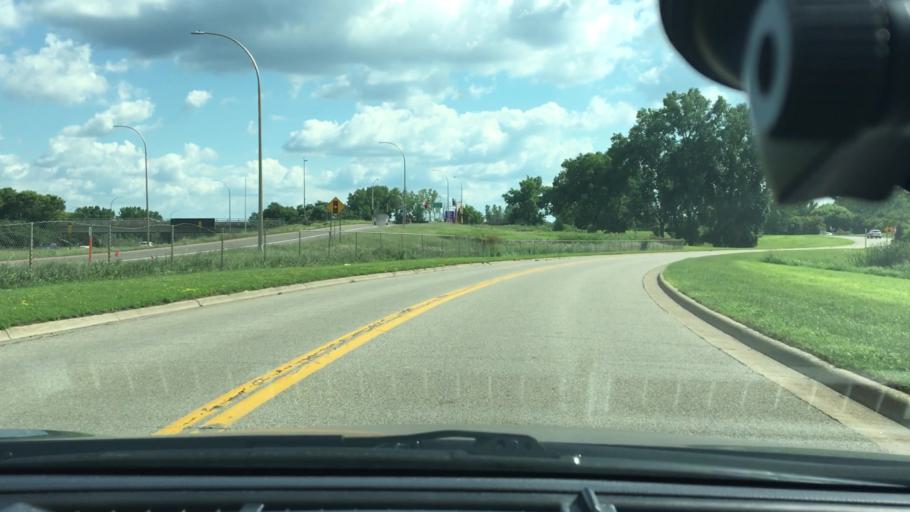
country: US
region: Minnesota
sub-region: Hennepin County
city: New Hope
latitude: 45.0459
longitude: -93.4014
